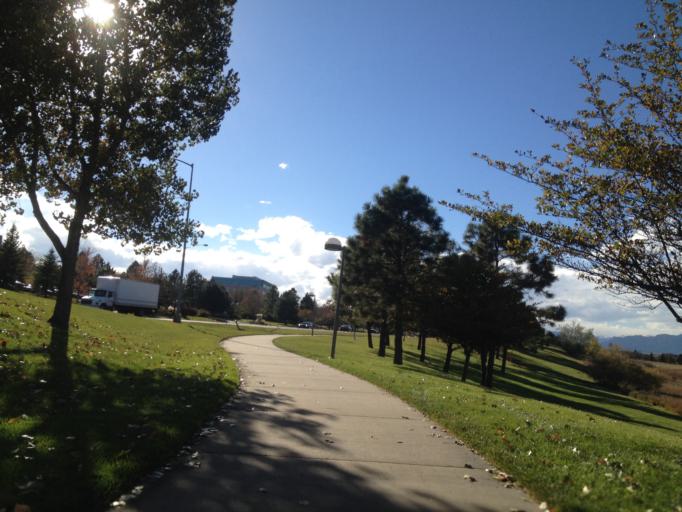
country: US
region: Colorado
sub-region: Broomfield County
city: Broomfield
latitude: 39.9169
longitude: -105.1184
